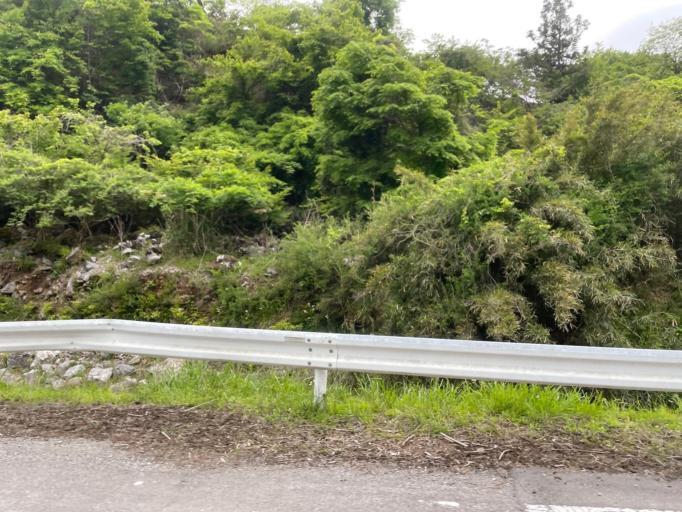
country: JP
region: Tochigi
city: Tanuma
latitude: 36.4616
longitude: 139.6026
